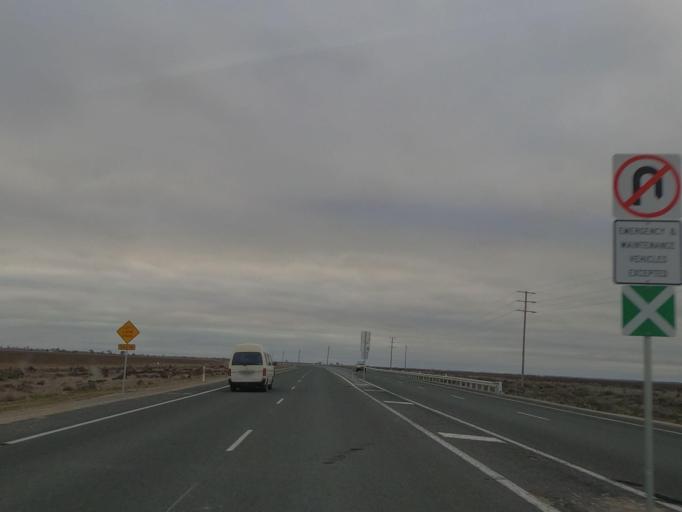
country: AU
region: Victoria
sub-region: Swan Hill
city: Swan Hill
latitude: -35.5114
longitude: 143.7249
